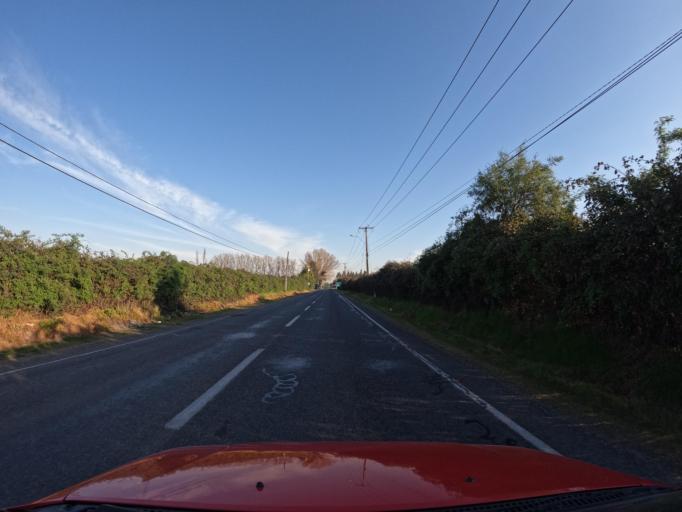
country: CL
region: Maule
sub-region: Provincia de Curico
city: Rauco
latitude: -34.9292
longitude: -71.2767
